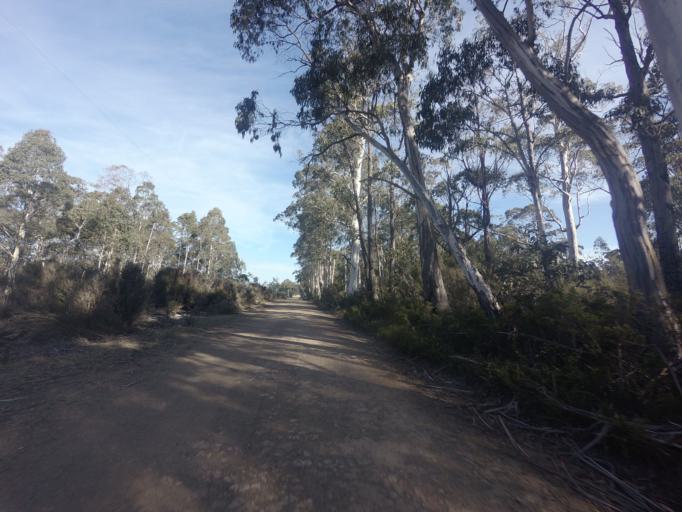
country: AU
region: Tasmania
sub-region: Sorell
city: Sorell
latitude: -42.5056
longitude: 147.4781
